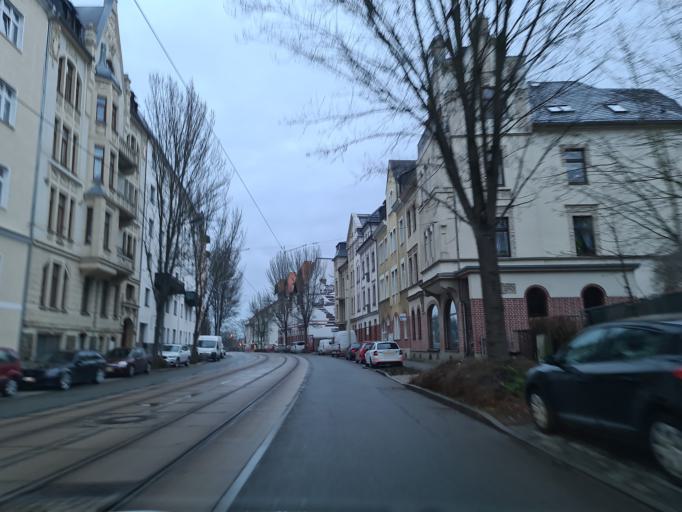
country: DE
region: Saxony
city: Plauen
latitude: 50.4946
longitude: 12.1118
